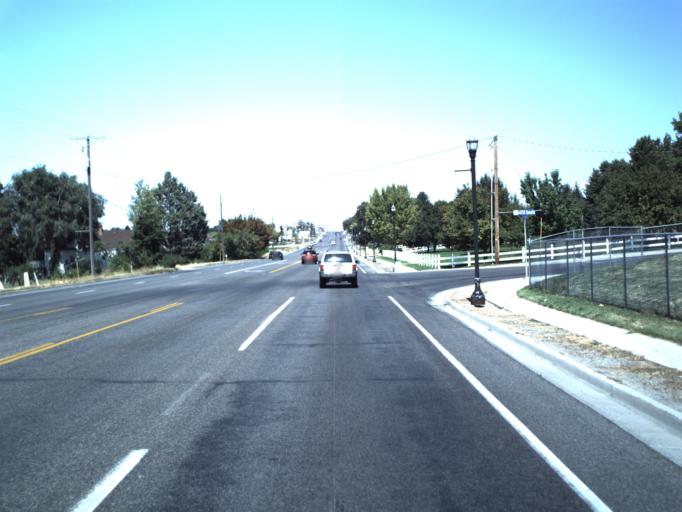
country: US
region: Utah
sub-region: Cache County
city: Richmond
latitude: 41.9125
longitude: -111.8145
